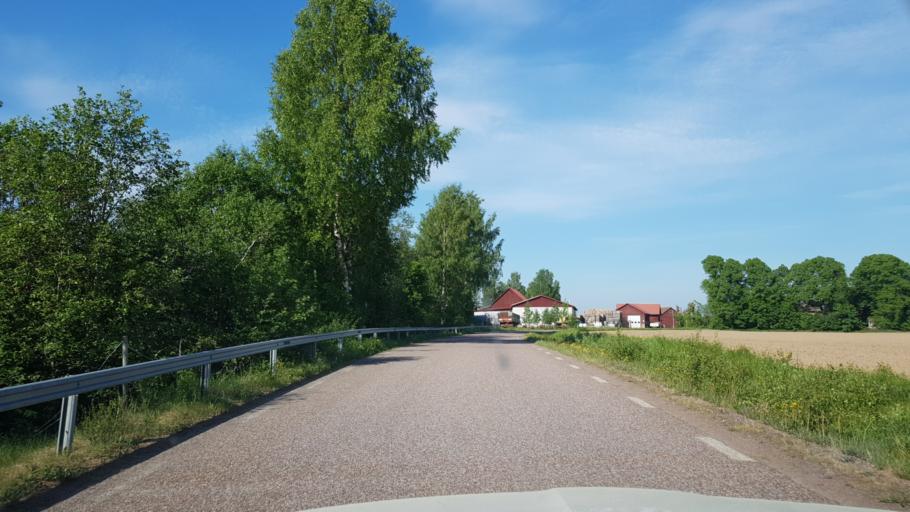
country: SE
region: Dalarna
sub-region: Hedemora Kommun
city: Langshyttan
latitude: 60.4057
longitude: 15.9063
